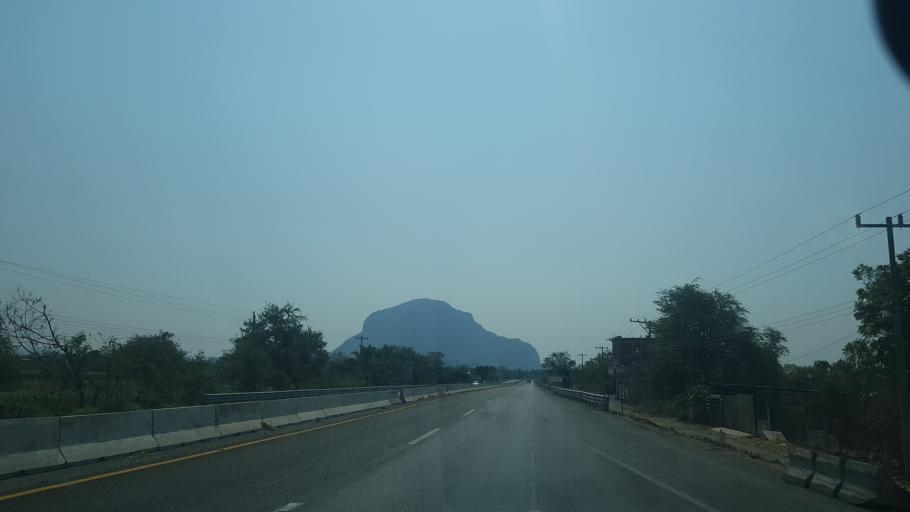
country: MX
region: Morelos
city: Amayuca
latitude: 18.7158
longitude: -98.7906
